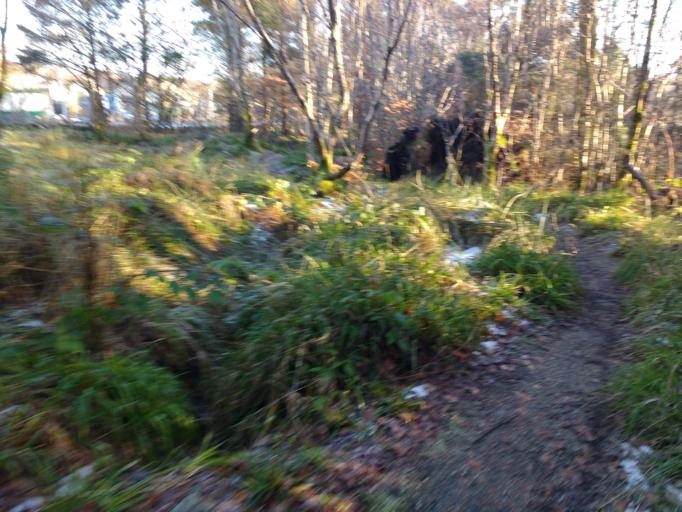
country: GB
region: Scotland
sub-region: Eilean Siar
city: Isle of Lewis
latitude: 58.2196
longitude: -6.3969
